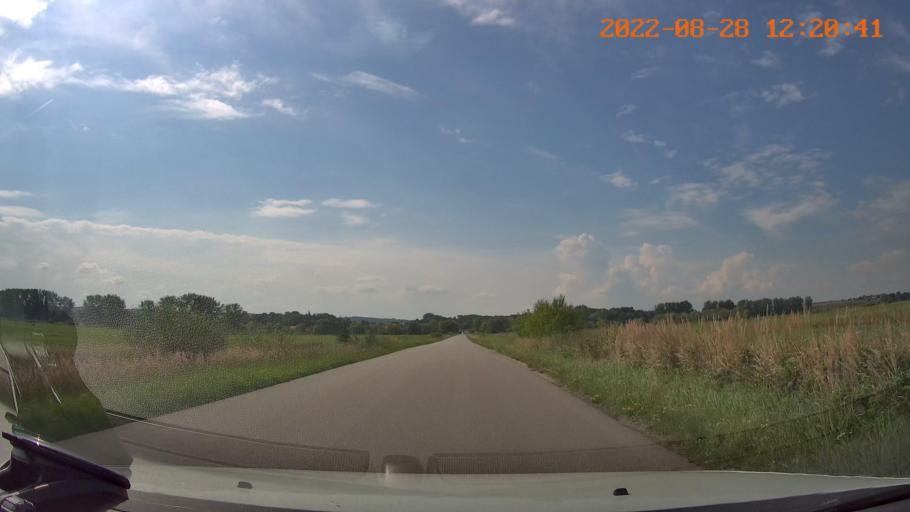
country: PL
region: Swietokrzyskie
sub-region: Powiat pinczowski
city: Zlota
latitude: 50.4291
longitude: 20.5665
